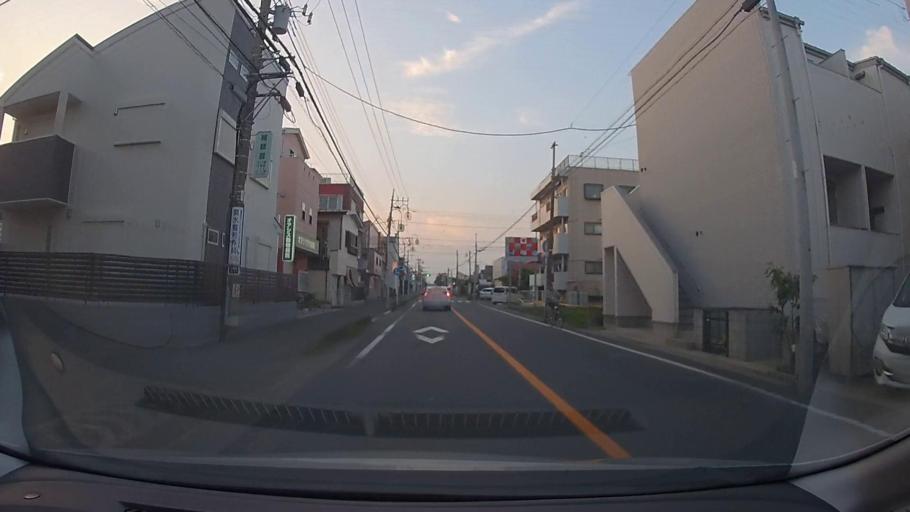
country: JP
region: Kanagawa
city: Minami-rinkan
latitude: 35.4748
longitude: 139.4553
